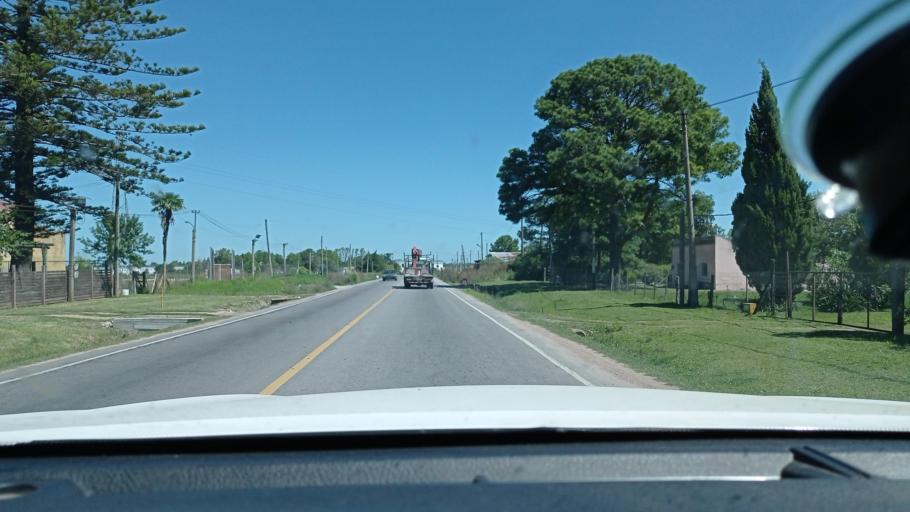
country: UY
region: Canelones
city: La Paz
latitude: -34.7798
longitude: -56.1674
